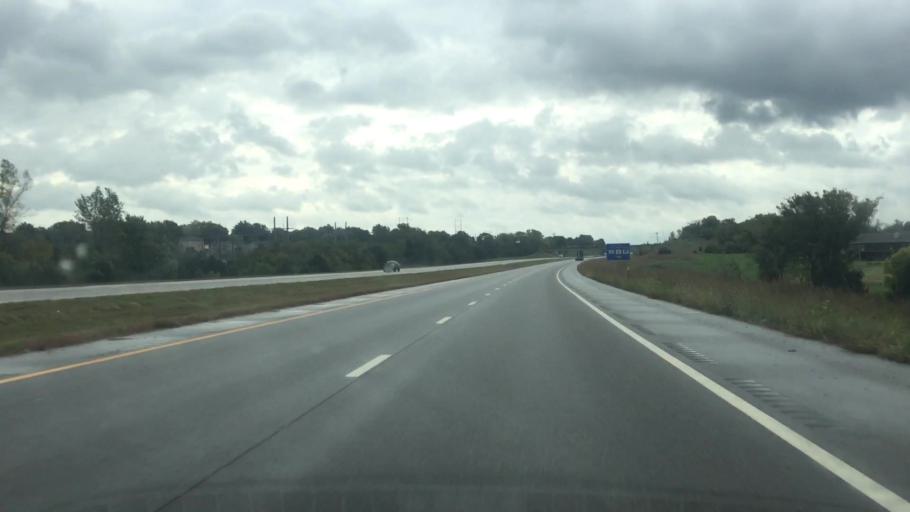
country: US
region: Kansas
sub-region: Miami County
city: Paola
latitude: 38.5582
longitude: -94.8673
